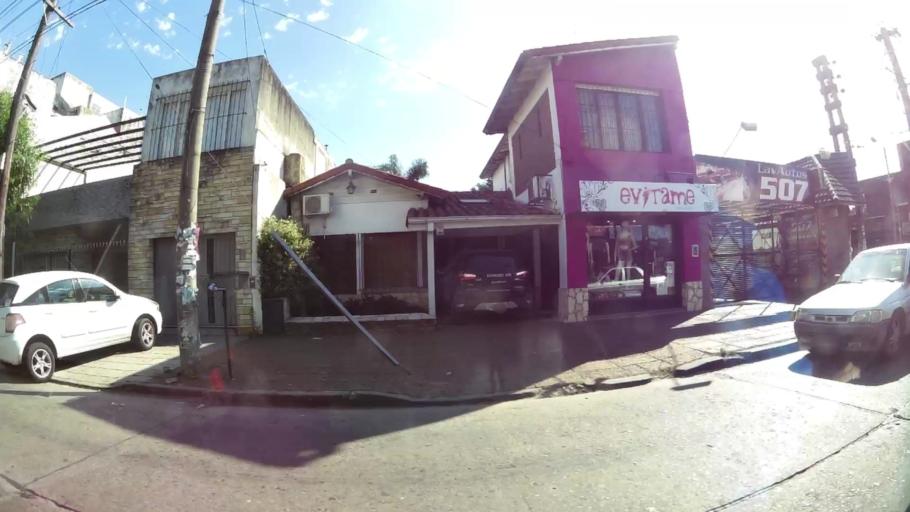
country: AR
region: Buenos Aires
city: San Justo
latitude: -34.6605
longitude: -58.5846
